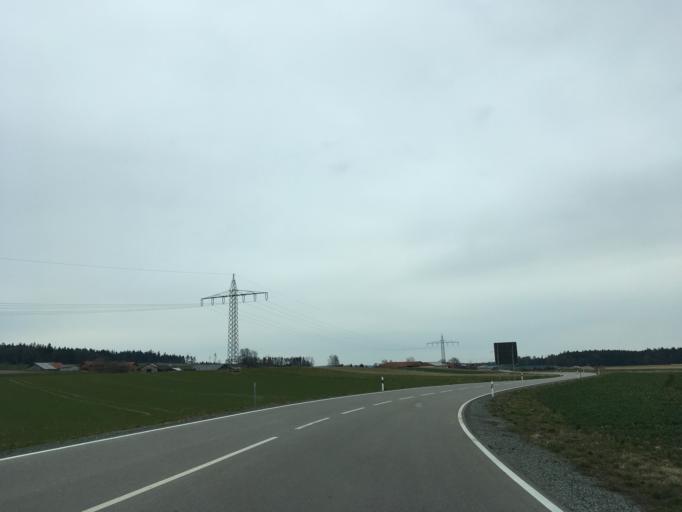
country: DE
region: Bavaria
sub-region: Upper Bavaria
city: Schnaitsee
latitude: 48.0695
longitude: 12.3888
